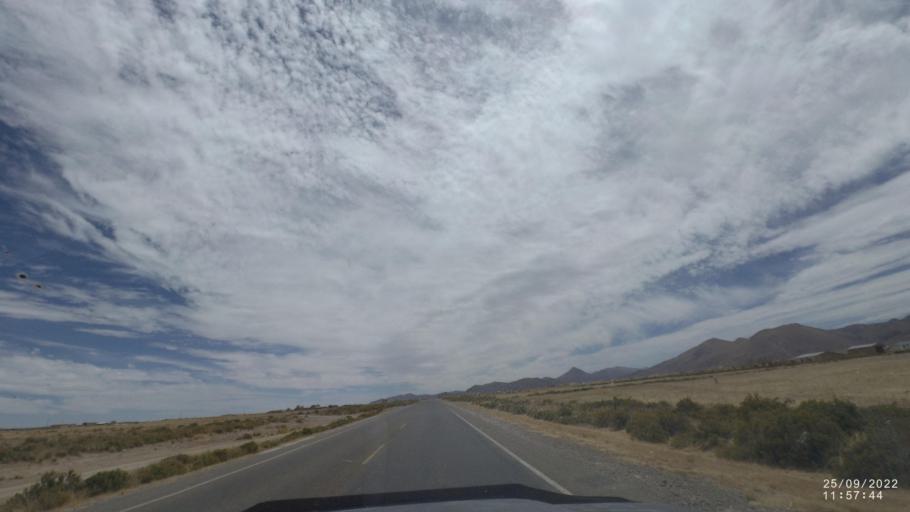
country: BO
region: Oruro
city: Challapata
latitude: -18.8175
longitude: -66.8307
